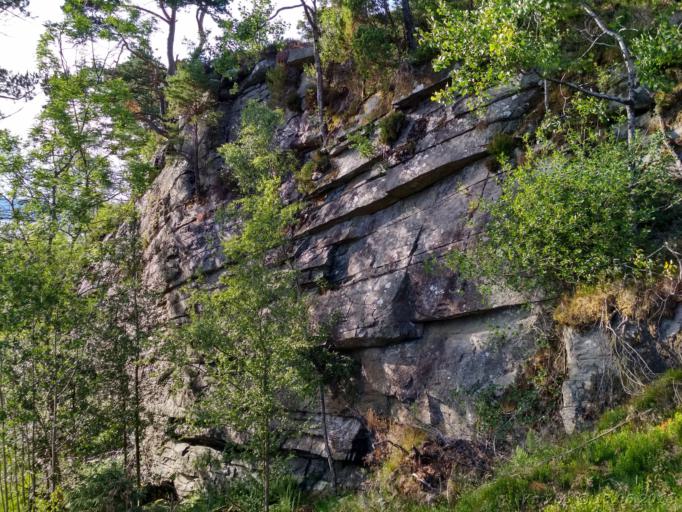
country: NO
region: Rogaland
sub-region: Finnoy
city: Judaberg
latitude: 59.2611
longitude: 5.8702
